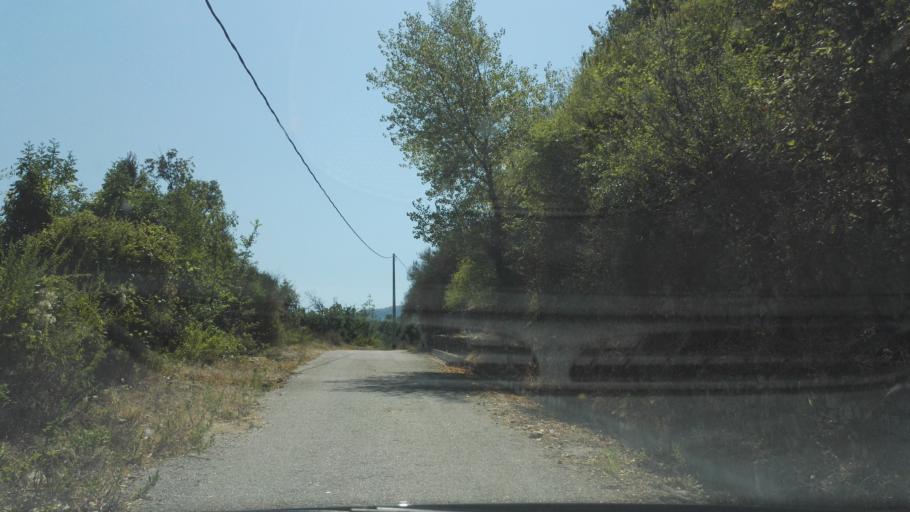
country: IT
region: Calabria
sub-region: Provincia di Reggio Calabria
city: Bivongi
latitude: 38.4895
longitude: 16.4207
